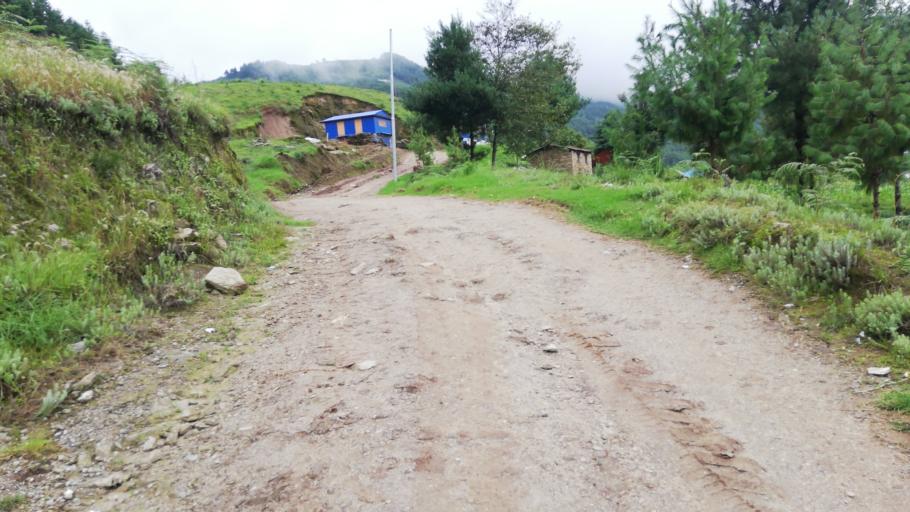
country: NP
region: Eastern Region
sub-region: Sagarmatha Zone
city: Namche Bazar
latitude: 27.4314
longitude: 86.6320
